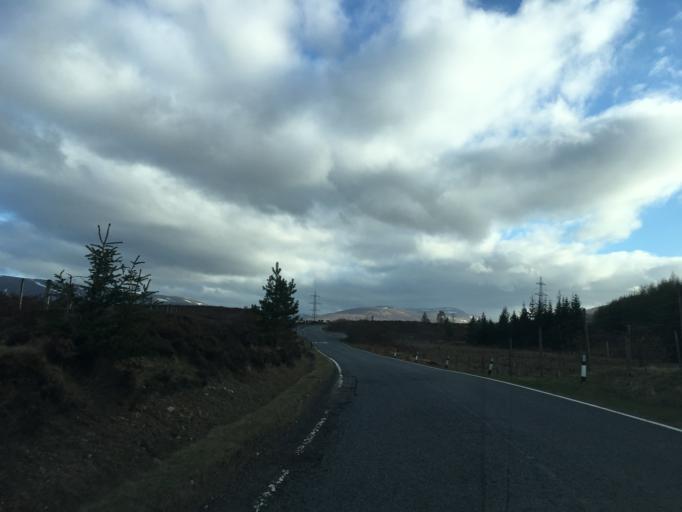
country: GB
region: Scotland
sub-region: Highland
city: Kingussie
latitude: 56.9671
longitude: -4.2395
